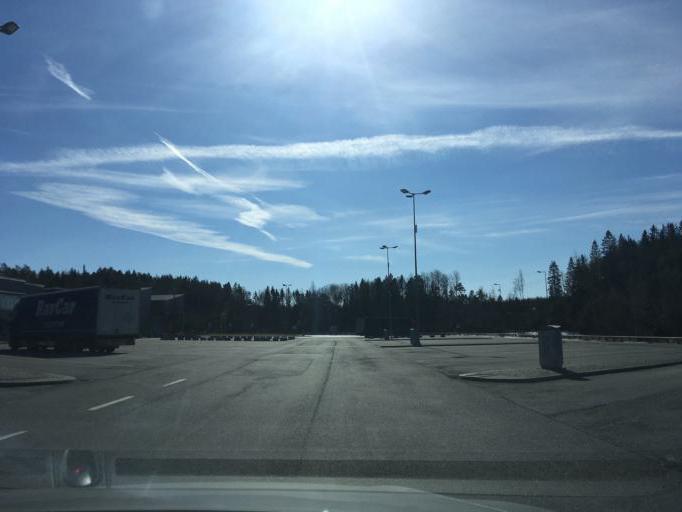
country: NO
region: Ostfold
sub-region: Sarpsborg
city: Skjeberg
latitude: 59.1092
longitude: 11.2613
